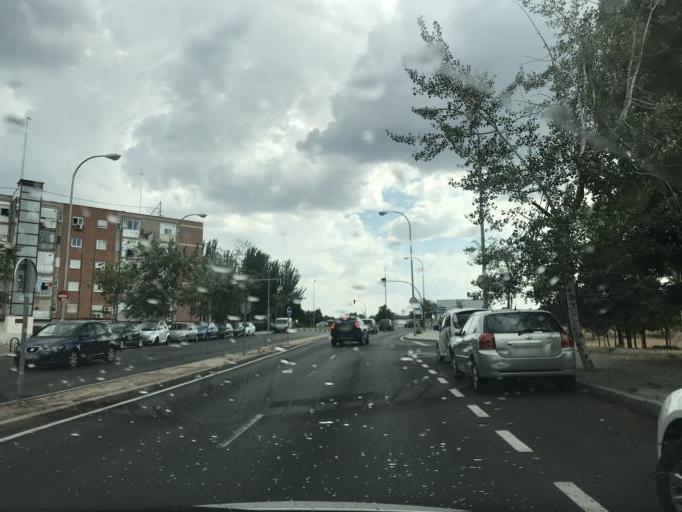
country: ES
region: Madrid
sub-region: Provincia de Madrid
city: Pinar de Chamartin
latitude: 40.4721
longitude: -3.6571
